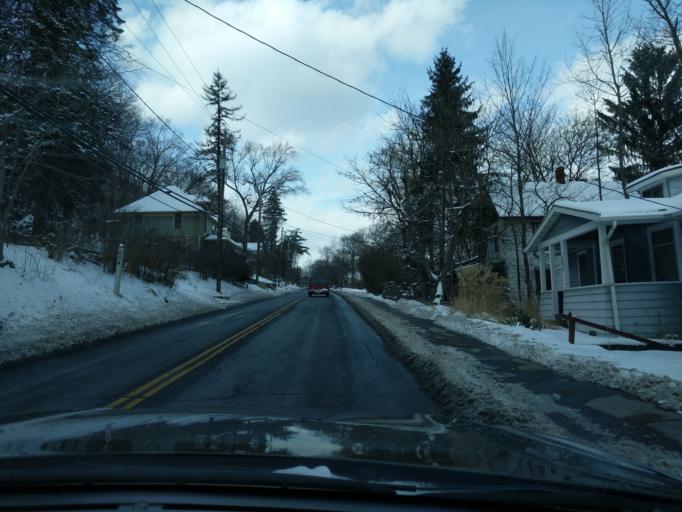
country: US
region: New York
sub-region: Tompkins County
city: Ithaca
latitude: 42.4470
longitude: -76.5166
